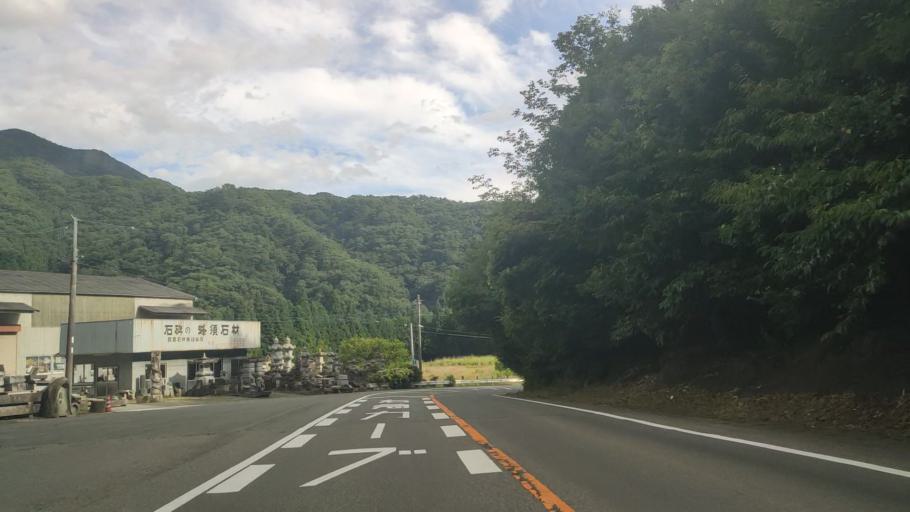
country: JP
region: Gunma
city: Kiryu
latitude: 36.5954
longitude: 139.4037
